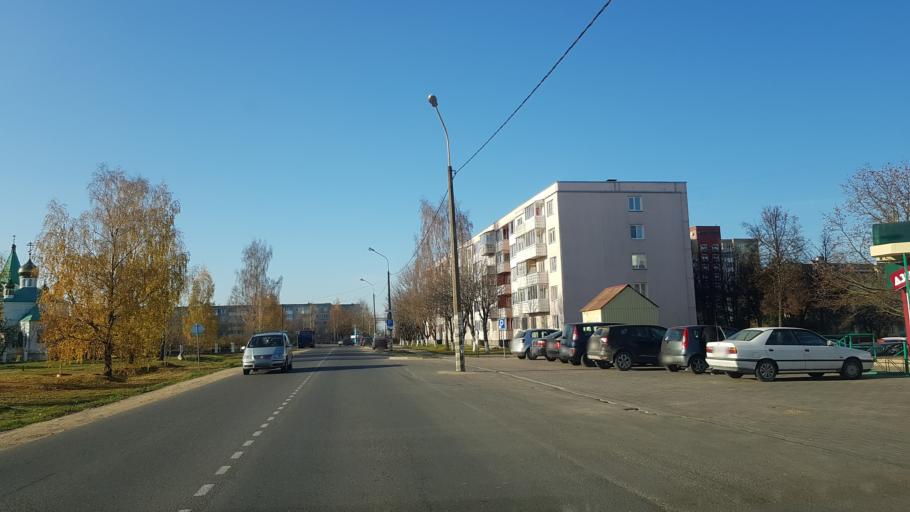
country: BY
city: Fanipol
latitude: 53.7382
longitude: 27.3191
